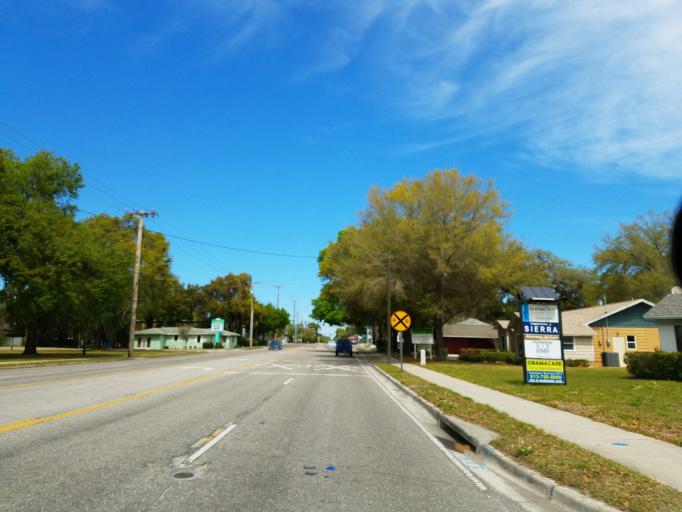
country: US
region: Florida
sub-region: Hillsborough County
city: Brandon
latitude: 27.9426
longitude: -82.2858
